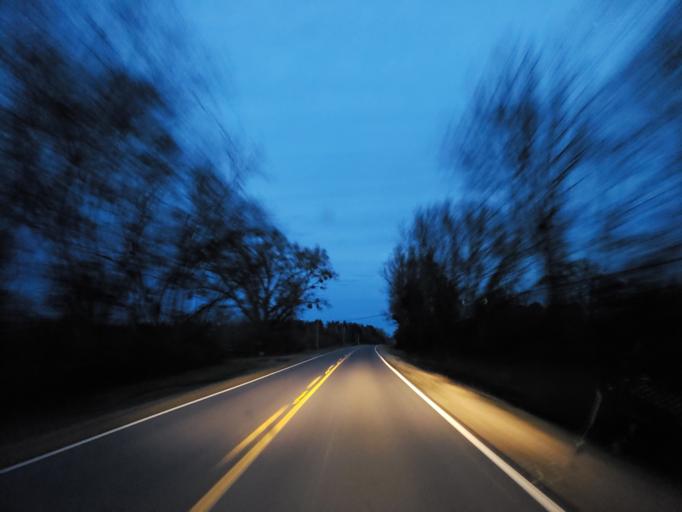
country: US
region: Alabama
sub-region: Greene County
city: Eutaw
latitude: 32.8869
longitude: -87.9427
